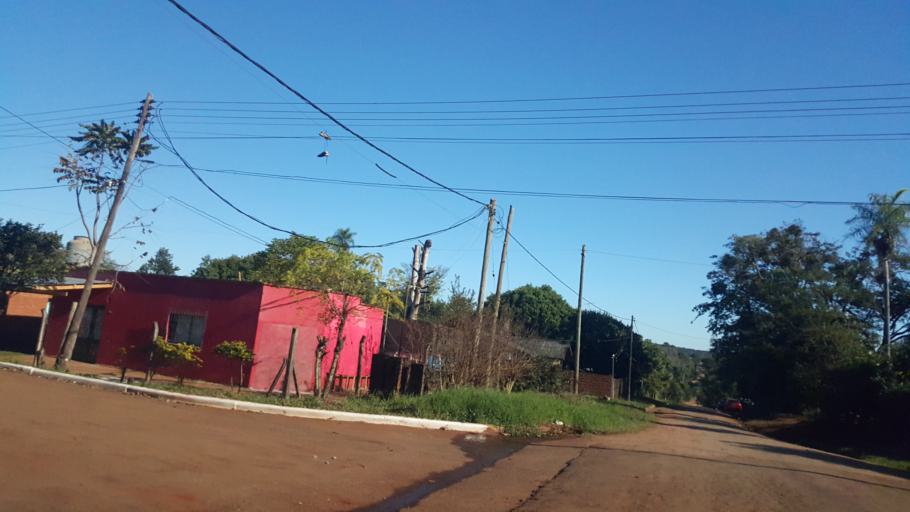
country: AR
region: Misiones
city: Gobernador Roca
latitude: -27.1905
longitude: -55.4720
